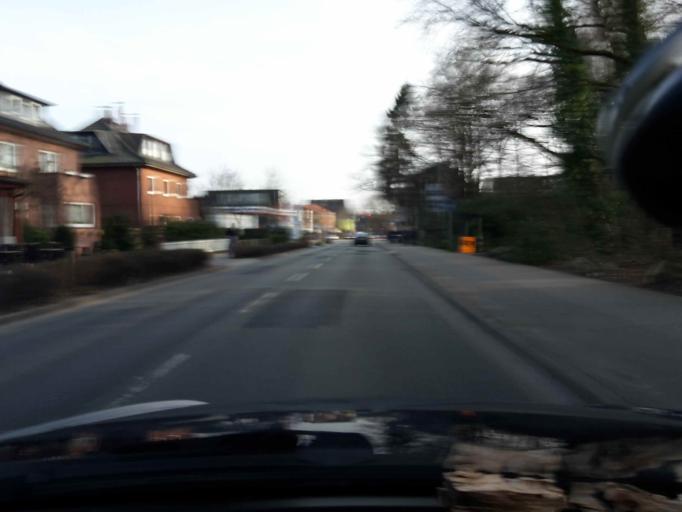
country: DE
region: Lower Saxony
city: Buchholz in der Nordheide
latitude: 53.3328
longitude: 9.8816
